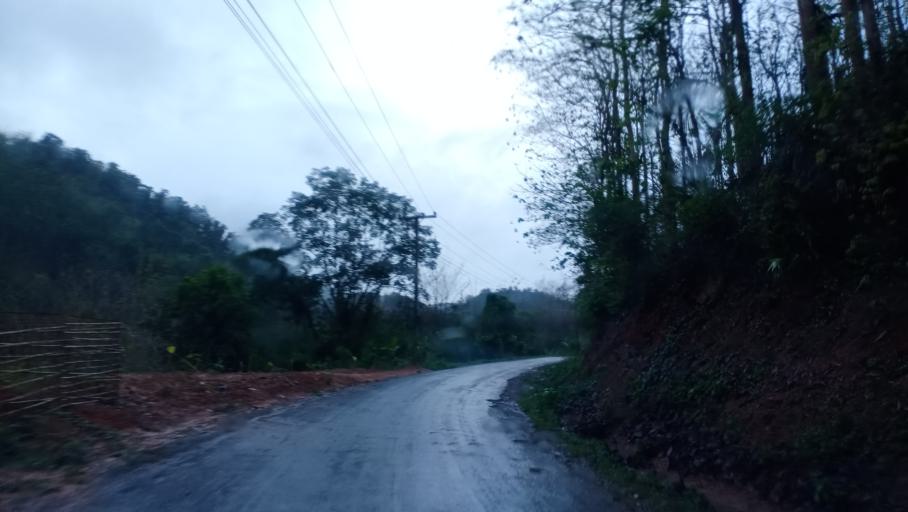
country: LA
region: Phongsali
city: Khoa
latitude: 21.0627
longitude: 102.4747
